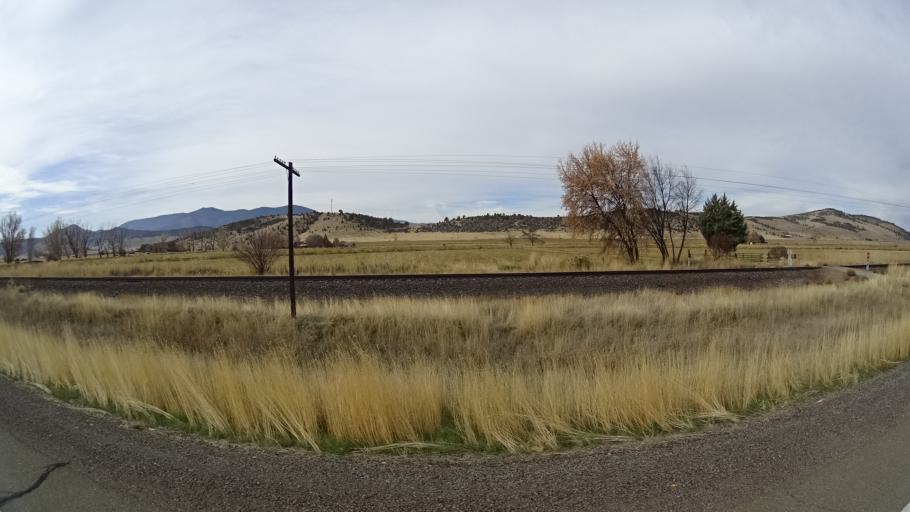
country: US
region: California
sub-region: Siskiyou County
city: Montague
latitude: 41.6570
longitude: -122.5203
